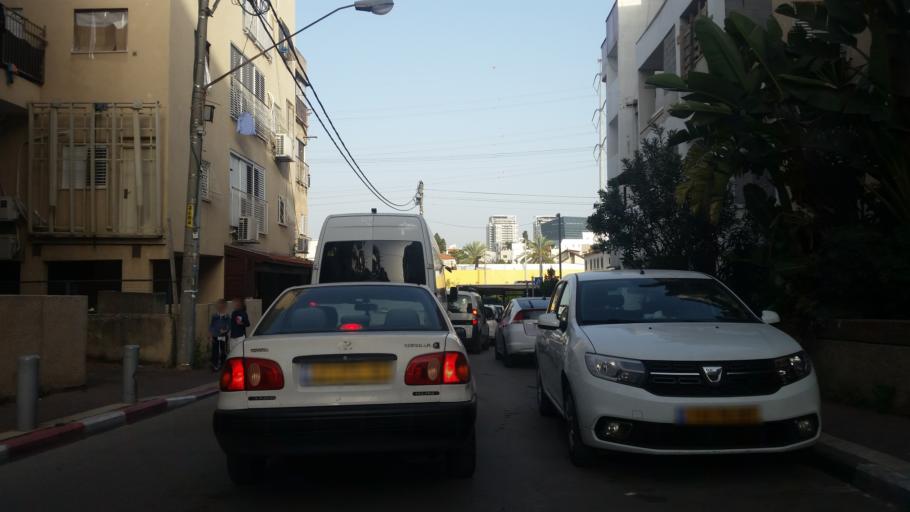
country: IL
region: Tel Aviv
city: Giv`at Shemu'el
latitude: 32.0747
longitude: 34.8418
